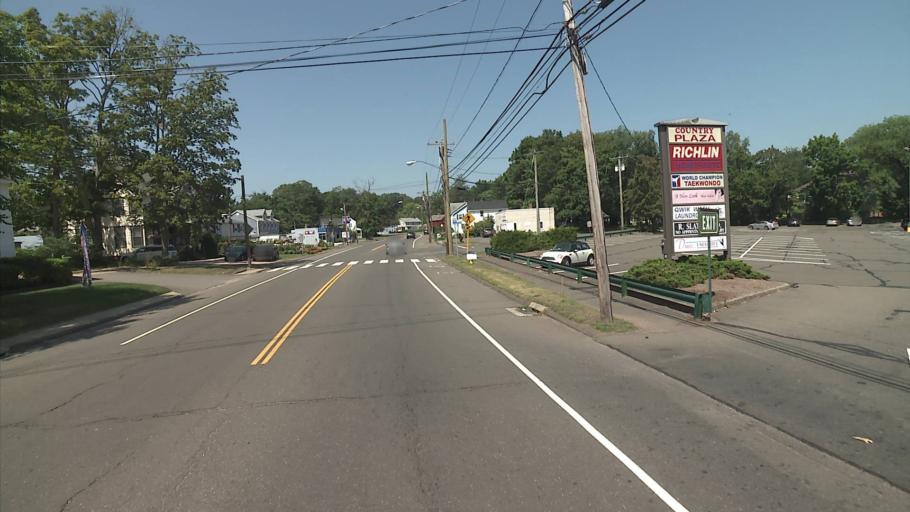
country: US
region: Connecticut
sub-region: New Haven County
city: Branford Center
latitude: 41.2776
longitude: -72.8222
